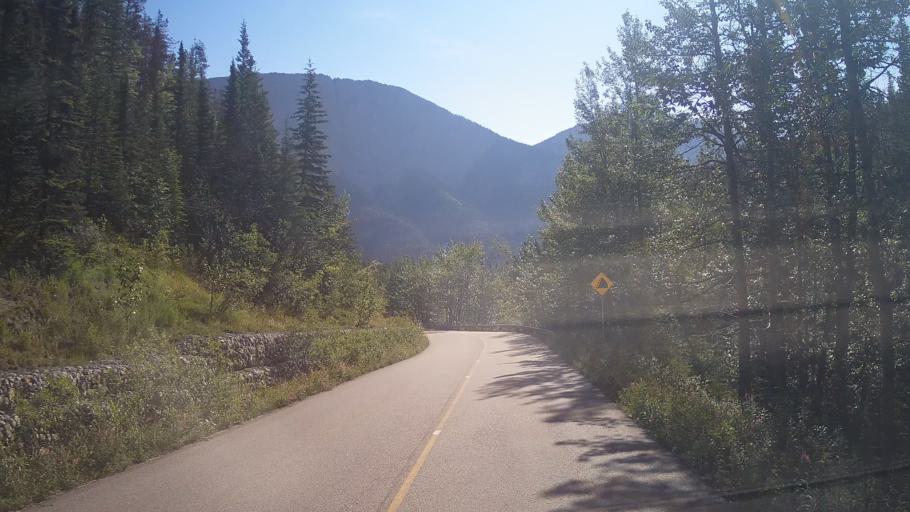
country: CA
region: Alberta
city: Hinton
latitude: 53.1768
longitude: -117.8538
